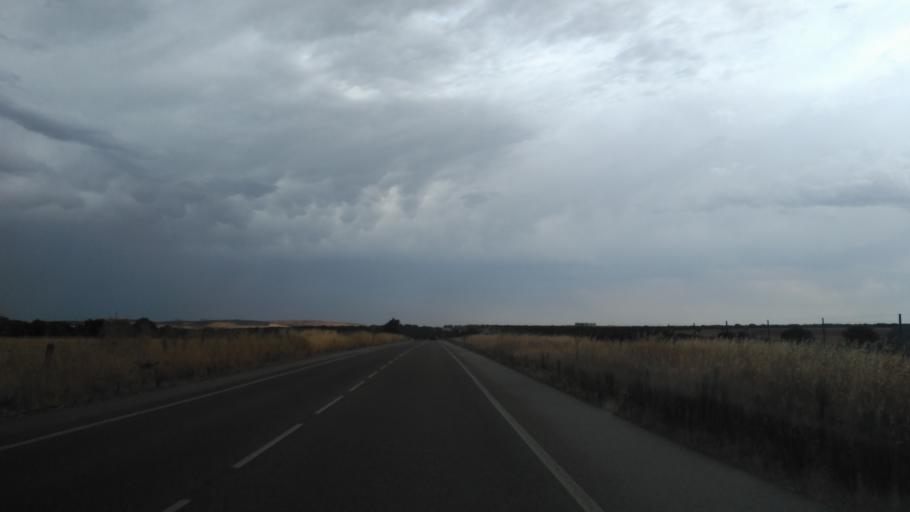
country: ES
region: Castille and Leon
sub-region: Provincia de Salamanca
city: San Pedro de Rozados
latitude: 40.8645
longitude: -5.7617
